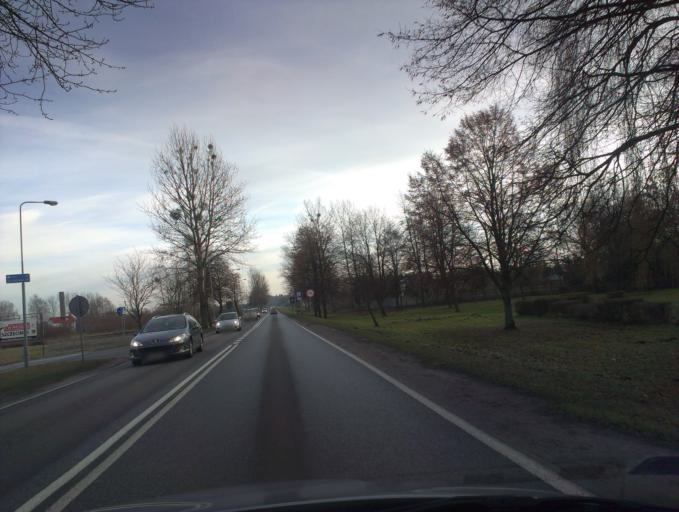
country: PL
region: West Pomeranian Voivodeship
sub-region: Powiat szczecinecki
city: Szczecinek
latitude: 53.7203
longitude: 16.6824
